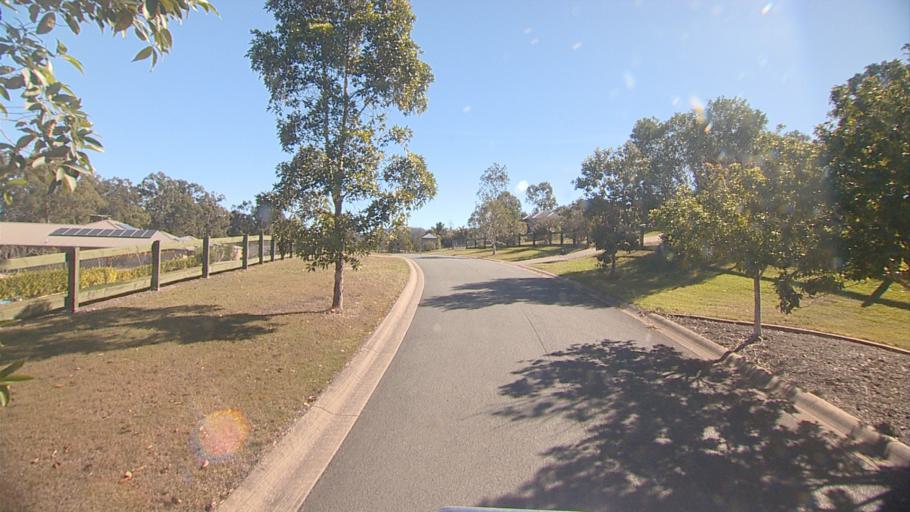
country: AU
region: Queensland
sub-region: Ipswich
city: Springfield Lakes
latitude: -27.7445
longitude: 152.9206
